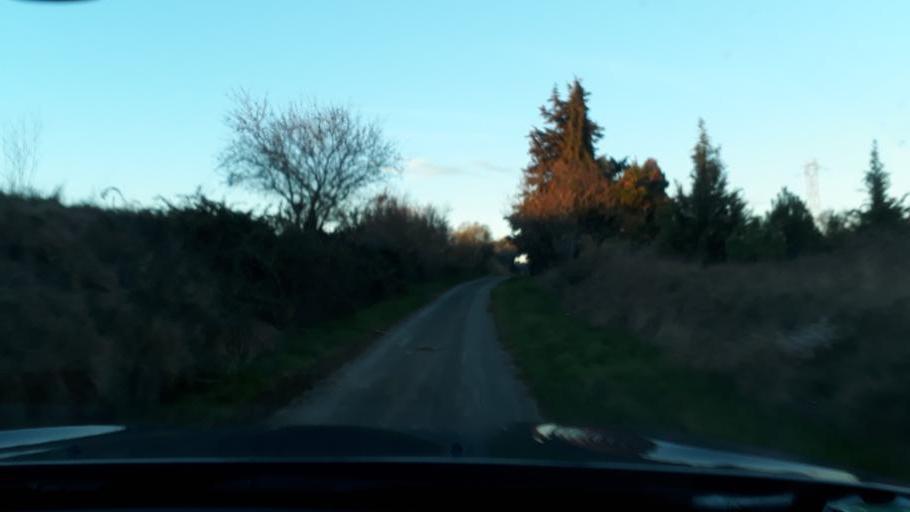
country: FR
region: Languedoc-Roussillon
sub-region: Departement de l'Herault
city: Florensac
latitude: 43.4100
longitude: 3.4591
